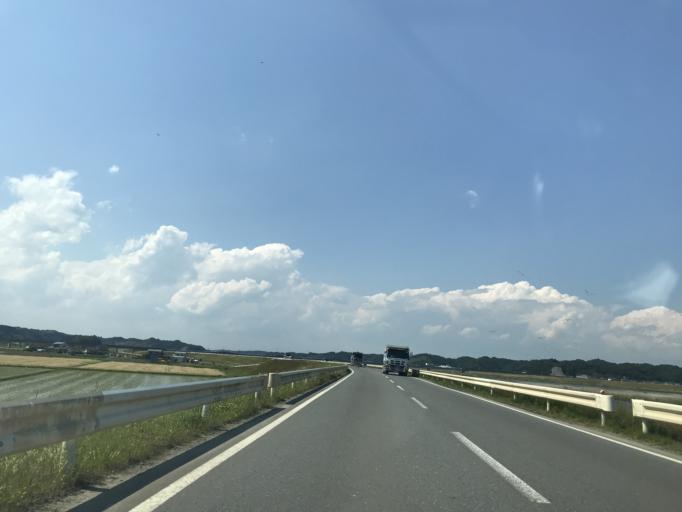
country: JP
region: Miyagi
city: Yamoto
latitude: 38.3824
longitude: 141.1683
